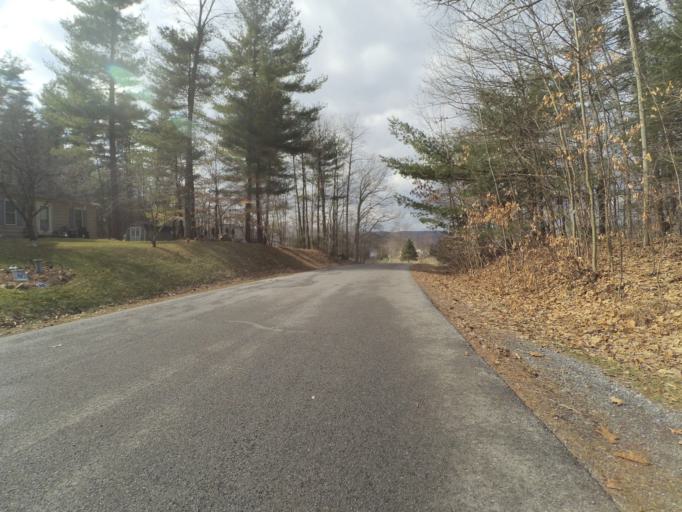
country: US
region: Pennsylvania
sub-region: Centre County
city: Stormstown
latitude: 40.7655
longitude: -78.0288
